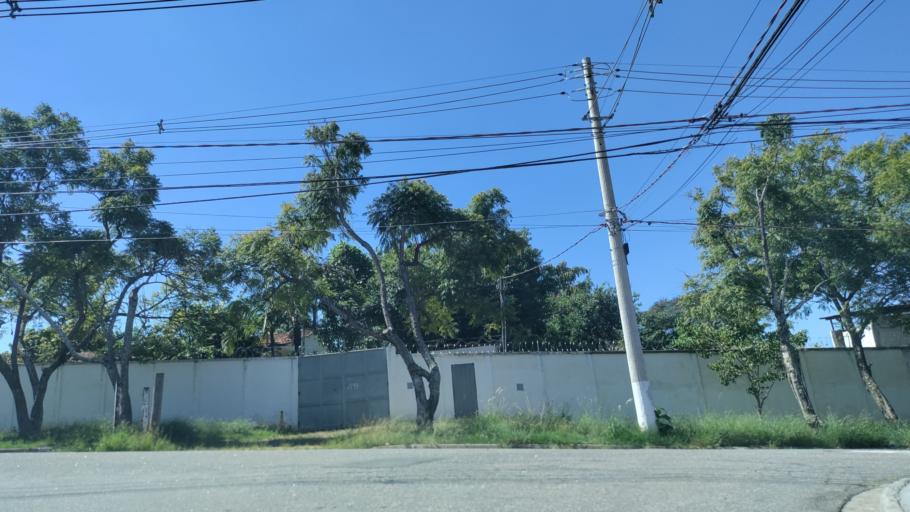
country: BR
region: Sao Paulo
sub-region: Sorocaba
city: Sorocaba
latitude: -23.4672
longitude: -47.4708
